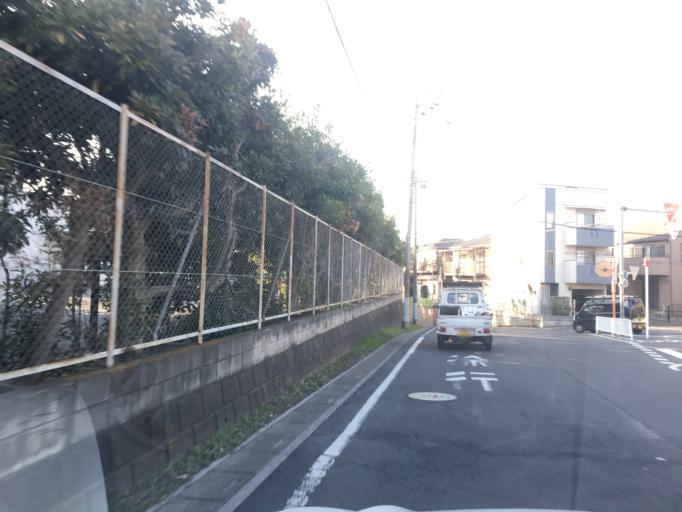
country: JP
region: Saitama
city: Kamifukuoka
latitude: 35.8667
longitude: 139.4983
